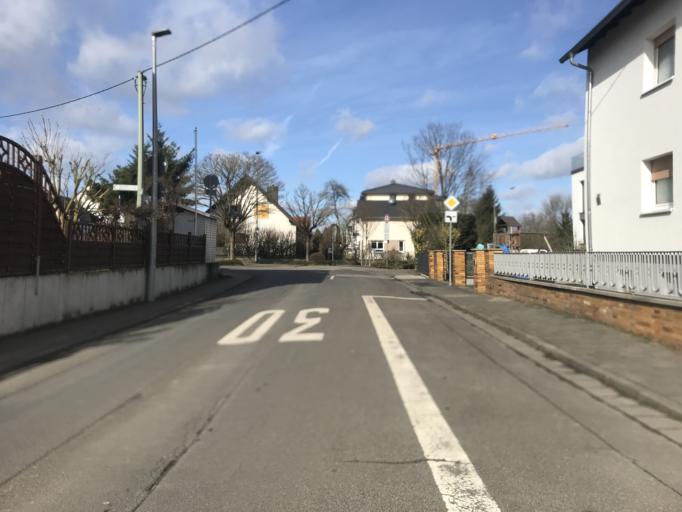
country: DE
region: Hesse
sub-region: Regierungsbezirk Darmstadt
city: Hochheim am Main
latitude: 50.0662
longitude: 8.3707
